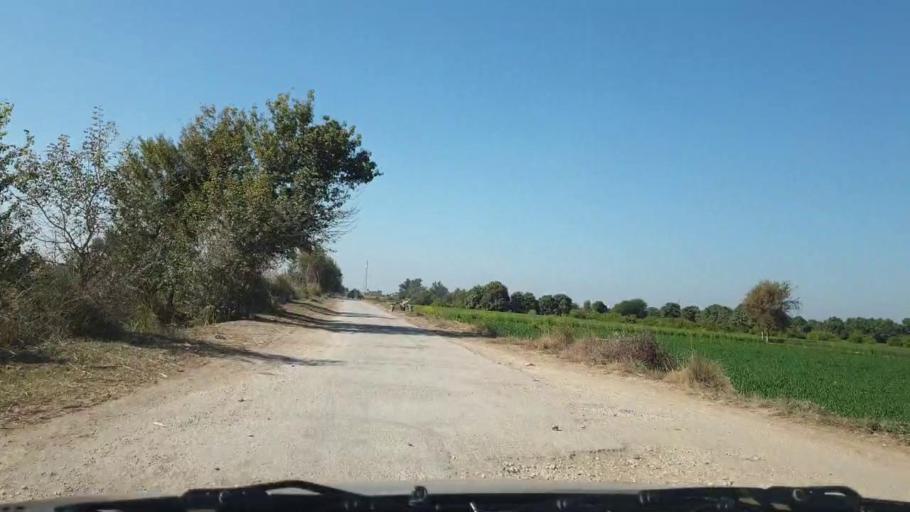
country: PK
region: Sindh
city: Khadro
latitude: 26.1290
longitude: 68.8139
